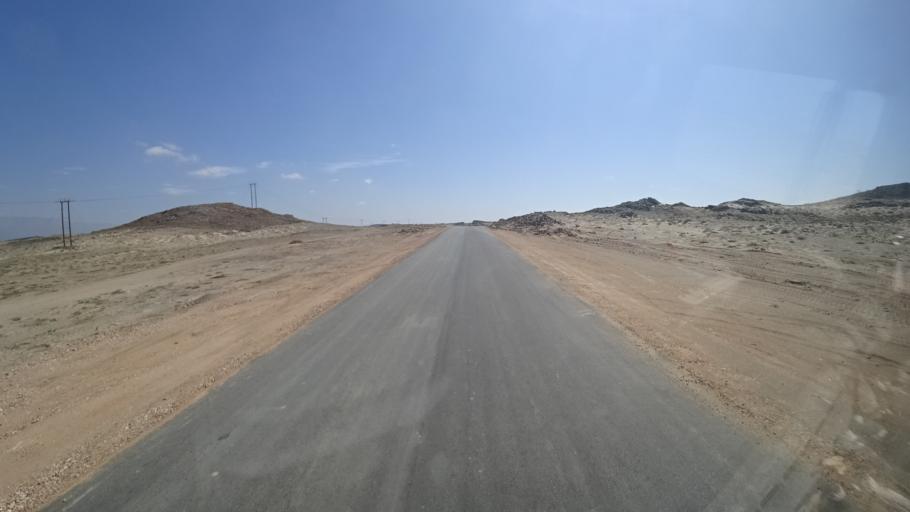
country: OM
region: Zufar
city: Salalah
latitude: 16.9643
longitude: 54.7633
